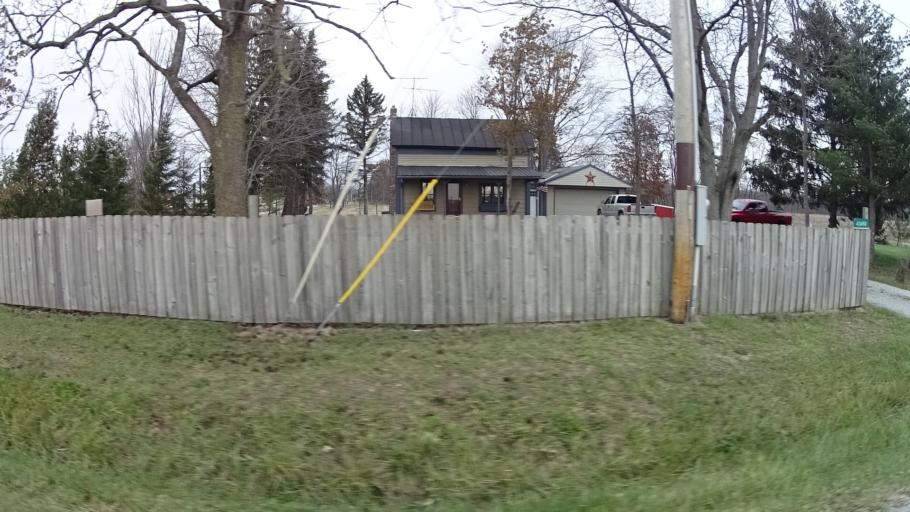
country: US
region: Ohio
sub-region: Lorain County
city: Wellington
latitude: 41.1544
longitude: -82.1692
